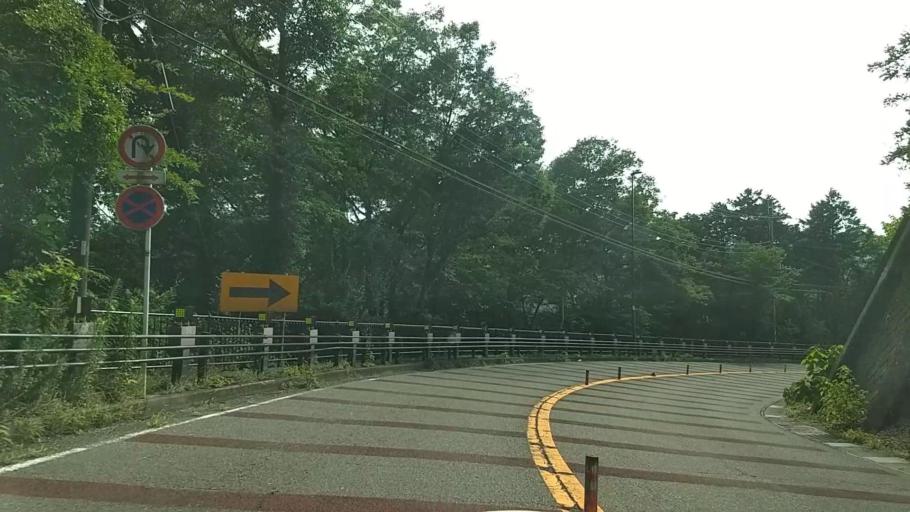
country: JP
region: Yamanashi
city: Uenohara
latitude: 35.6152
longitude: 139.2173
